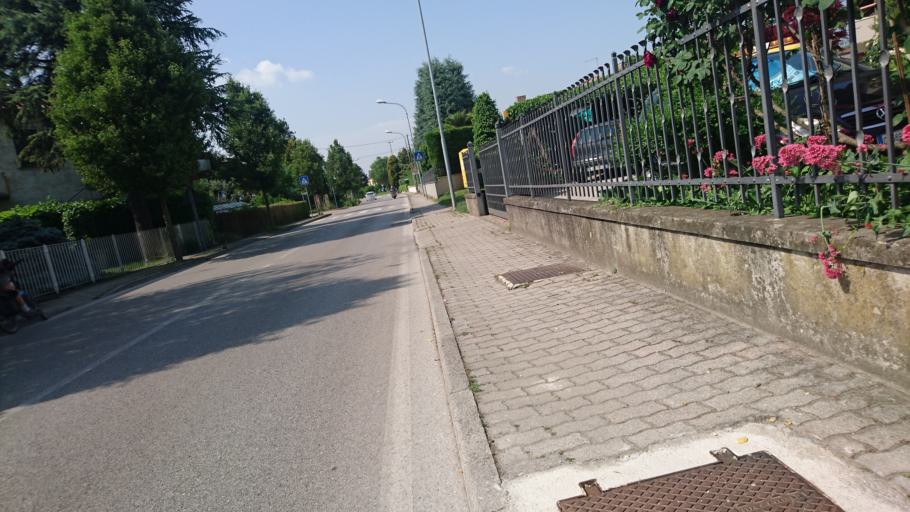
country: IT
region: Veneto
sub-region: Provincia di Venezia
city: Vigonovo
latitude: 45.3884
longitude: 12.0075
